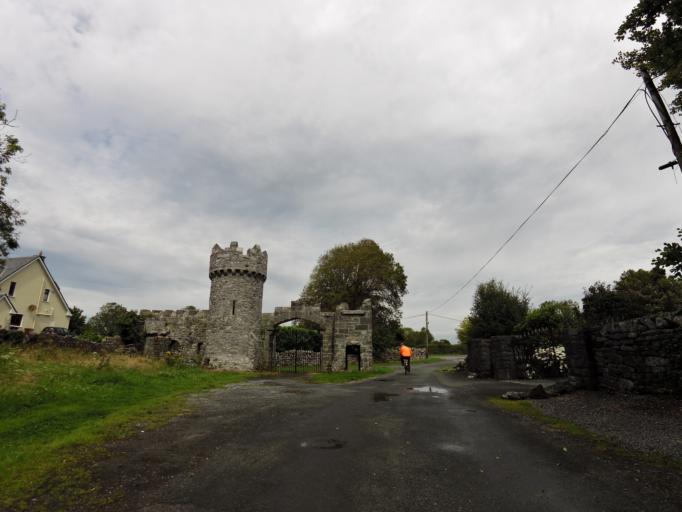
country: IE
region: Connaught
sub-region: County Galway
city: Gaillimh
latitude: 53.3001
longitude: -9.0726
